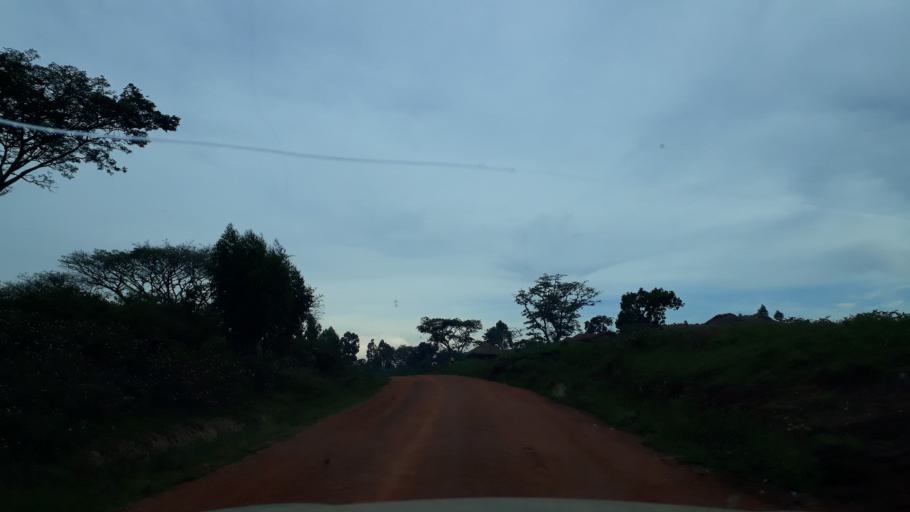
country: UG
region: Northern Region
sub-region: Zombo District
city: Paidha
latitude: 2.2046
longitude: 30.7460
